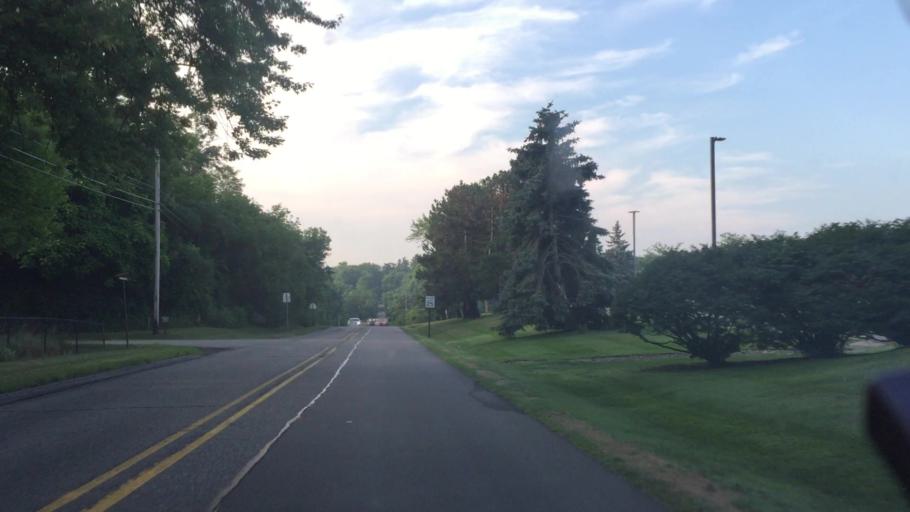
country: US
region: Michigan
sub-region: Oakland County
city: Bloomfield Hills
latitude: 42.5951
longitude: -83.2476
